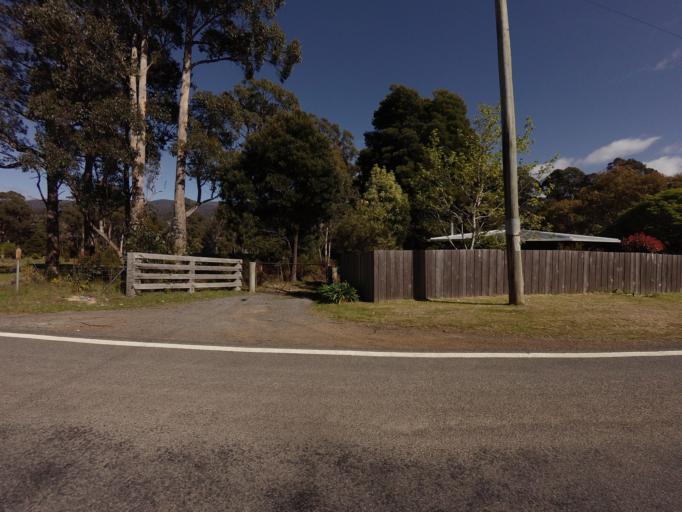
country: AU
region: Tasmania
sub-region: Derwent Valley
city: New Norfolk
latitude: -42.6887
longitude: 146.7175
